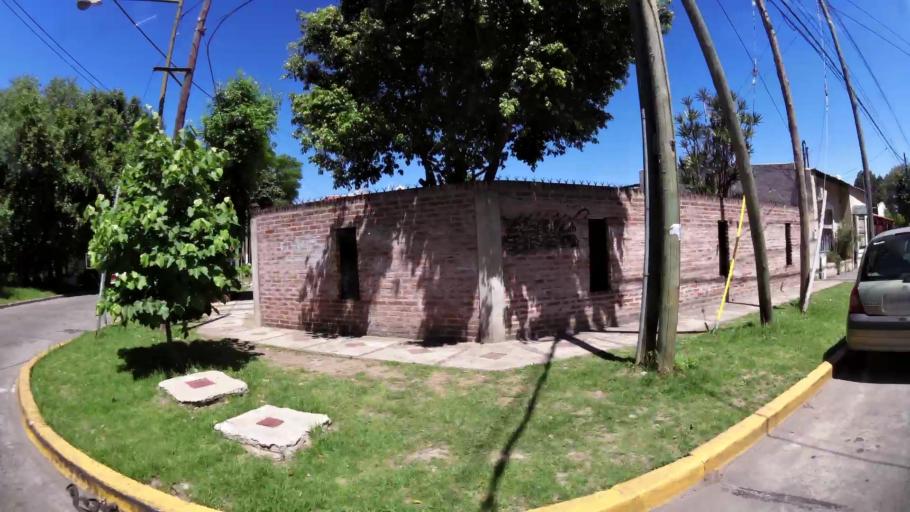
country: AR
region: Buenos Aires
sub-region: Partido de San Isidro
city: San Isidro
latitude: -34.5032
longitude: -58.5445
